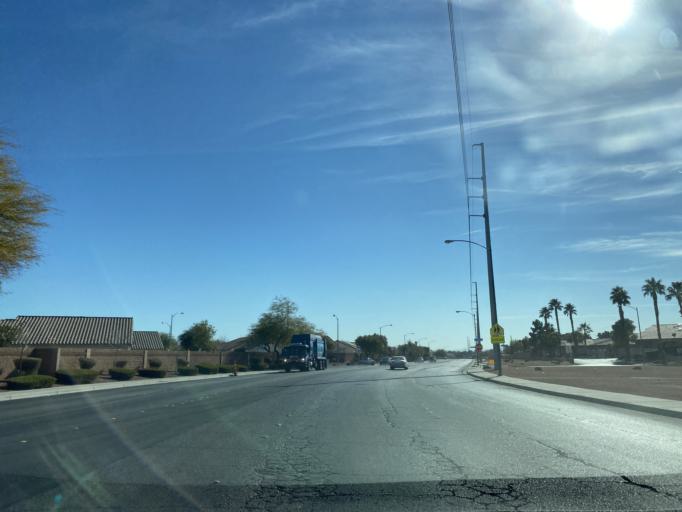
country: US
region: Nevada
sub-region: Clark County
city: North Las Vegas
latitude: 36.2477
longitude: -115.1439
